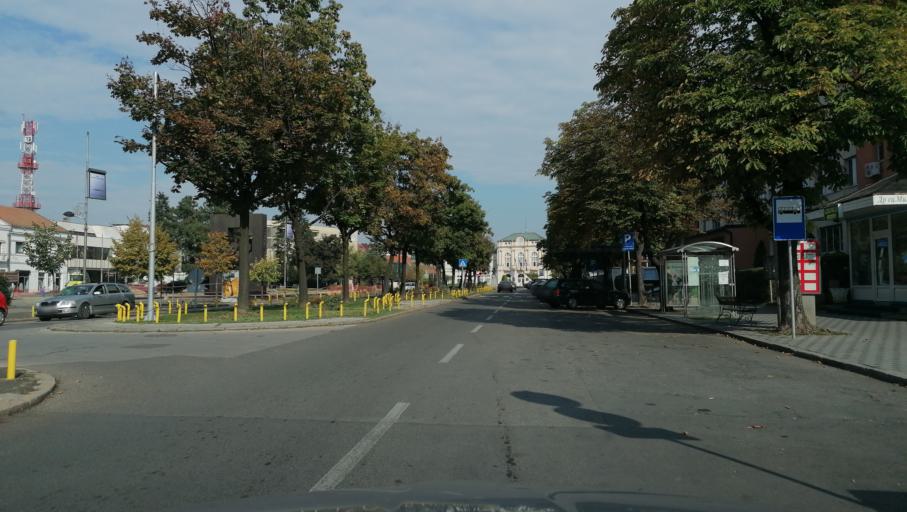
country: BA
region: Republika Srpska
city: Bijeljina
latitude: 44.7564
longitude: 19.2158
